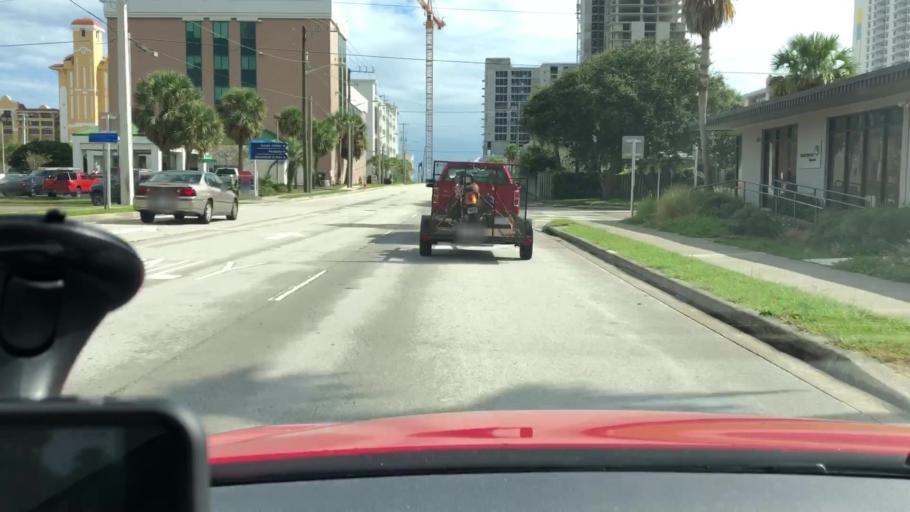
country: US
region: Florida
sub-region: Volusia County
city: Daytona Beach
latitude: 29.2330
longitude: -81.0141
